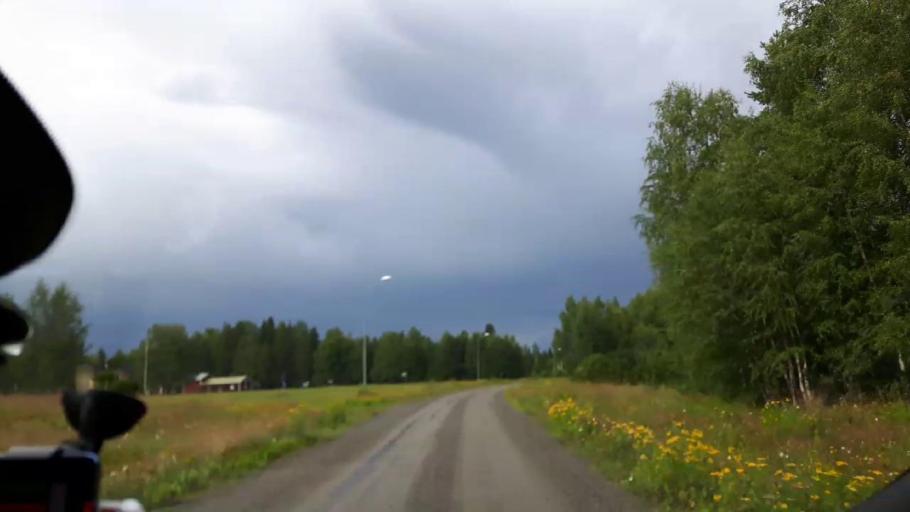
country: SE
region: Jaemtland
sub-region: Stroemsunds Kommun
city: Stroemsund
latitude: 64.0575
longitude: 15.8907
